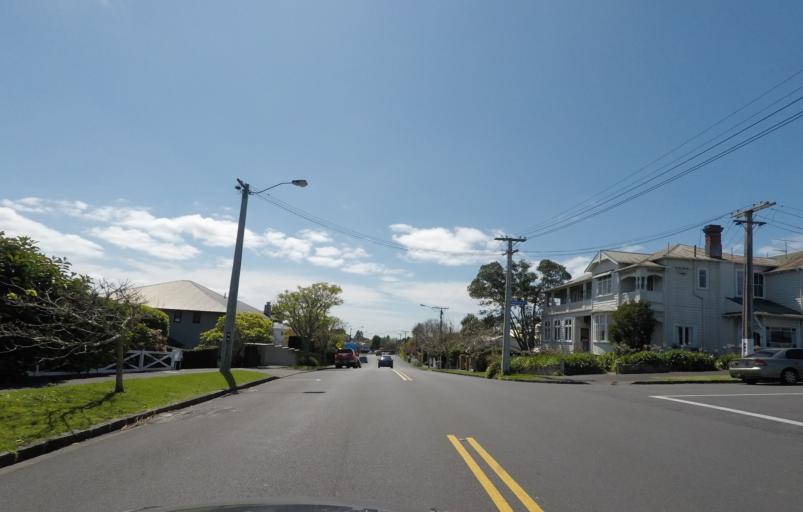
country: NZ
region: Auckland
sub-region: Auckland
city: Auckland
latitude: -36.8839
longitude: 174.8091
